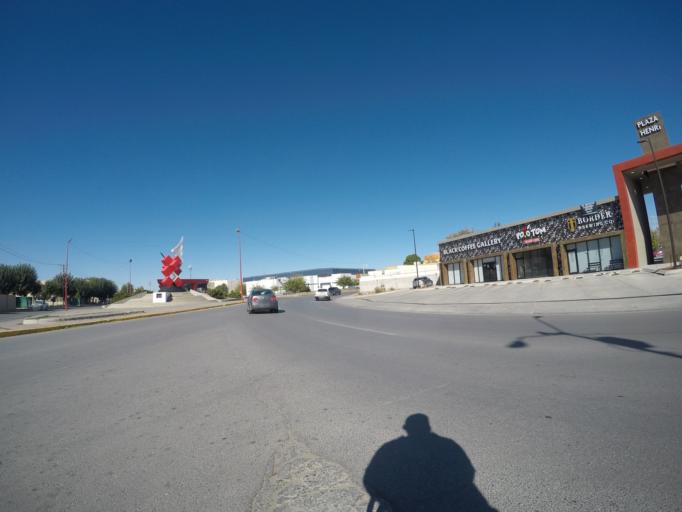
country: MX
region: Chihuahua
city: Ciudad Juarez
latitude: 31.7411
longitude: -106.4431
